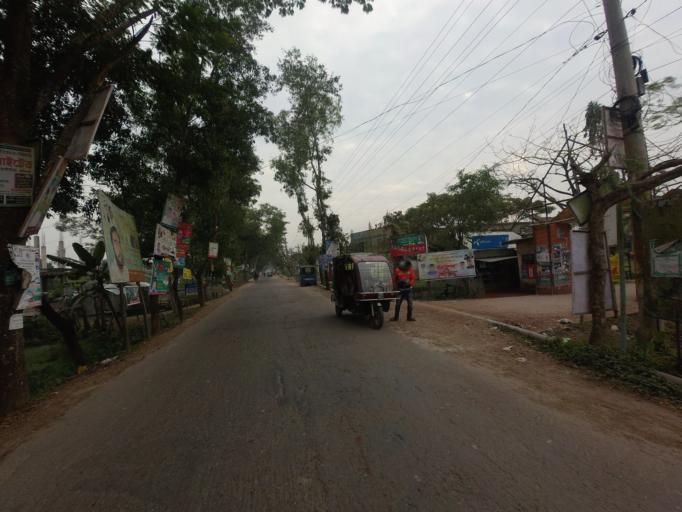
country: BD
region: Barisal
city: Nalchiti
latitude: 22.4653
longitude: 90.3752
